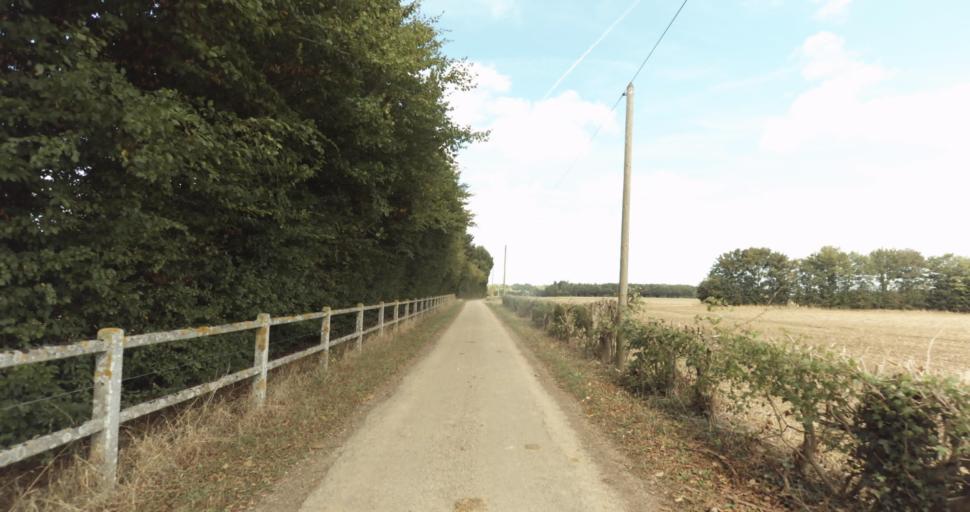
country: FR
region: Lower Normandy
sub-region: Departement de l'Orne
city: Gace
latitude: 48.8897
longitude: 0.3632
